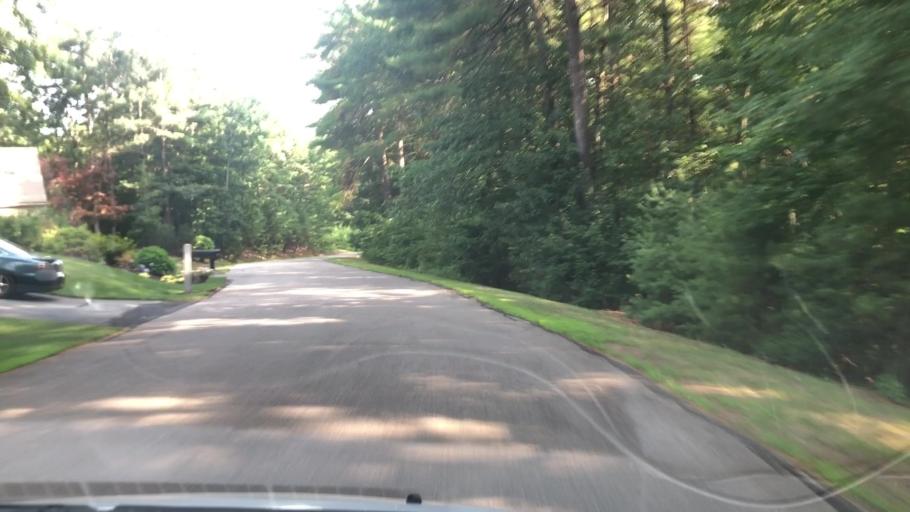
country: US
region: New Hampshire
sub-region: Hillsborough County
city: Milford
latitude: 42.8410
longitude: -71.6259
